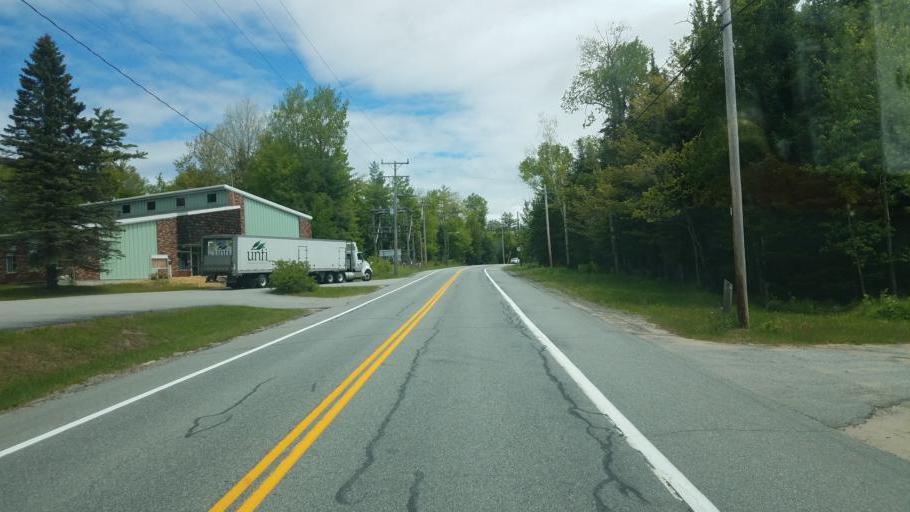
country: US
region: New York
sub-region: Hamilton County
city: Lake Pleasant
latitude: 43.8087
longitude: -74.6546
